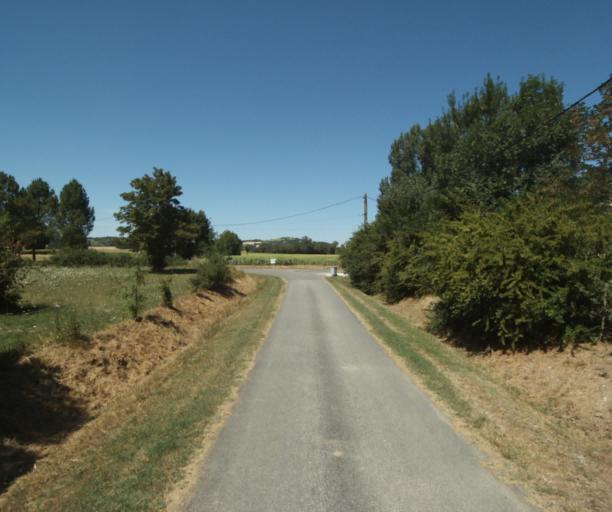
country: FR
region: Midi-Pyrenees
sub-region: Departement de la Haute-Garonne
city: Revel
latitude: 43.4792
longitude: 1.9459
